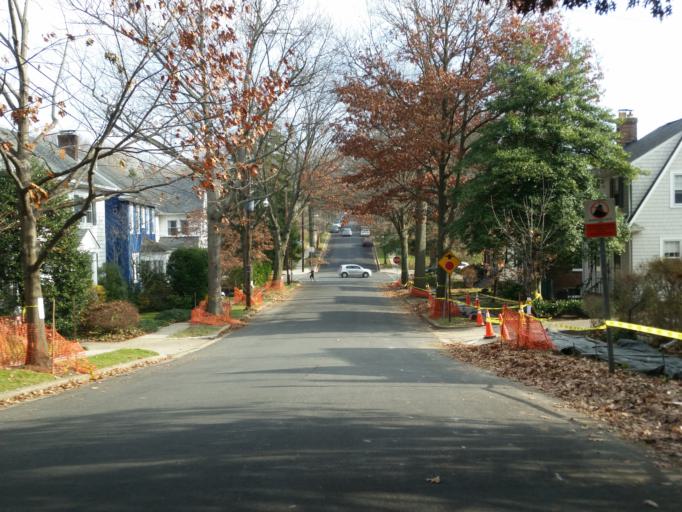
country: US
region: Maryland
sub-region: Montgomery County
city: Chevy Chase
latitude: 38.9640
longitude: -77.0712
